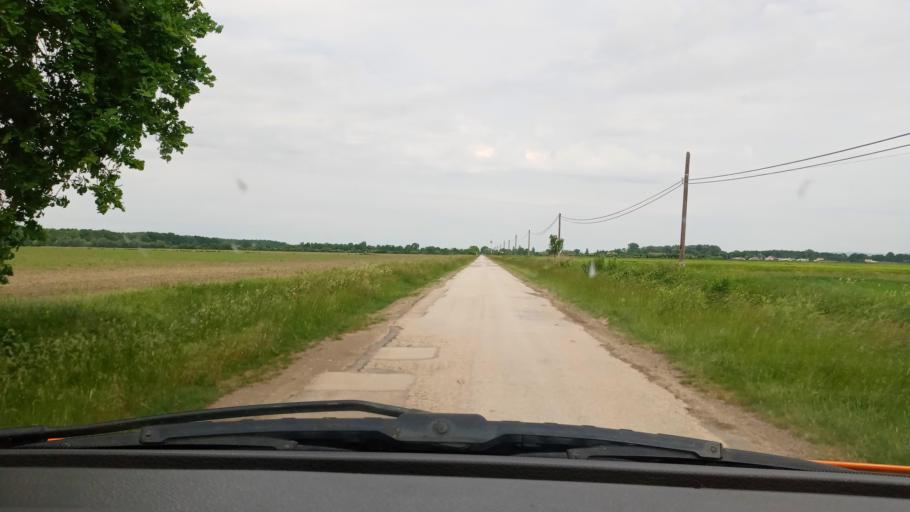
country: HU
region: Baranya
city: Vajszlo
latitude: 45.9146
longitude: 18.0264
